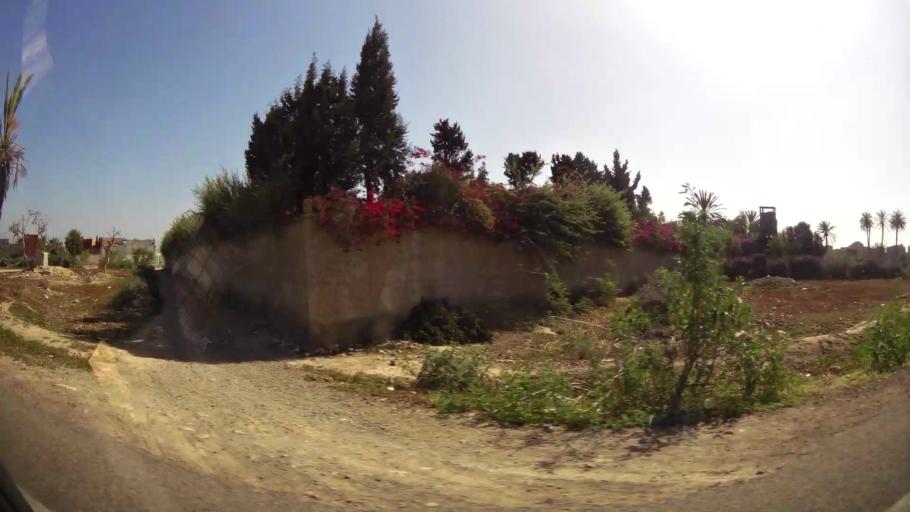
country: MA
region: Souss-Massa-Draa
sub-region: Inezgane-Ait Mellou
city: Inezgane
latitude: 30.3195
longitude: -9.5270
